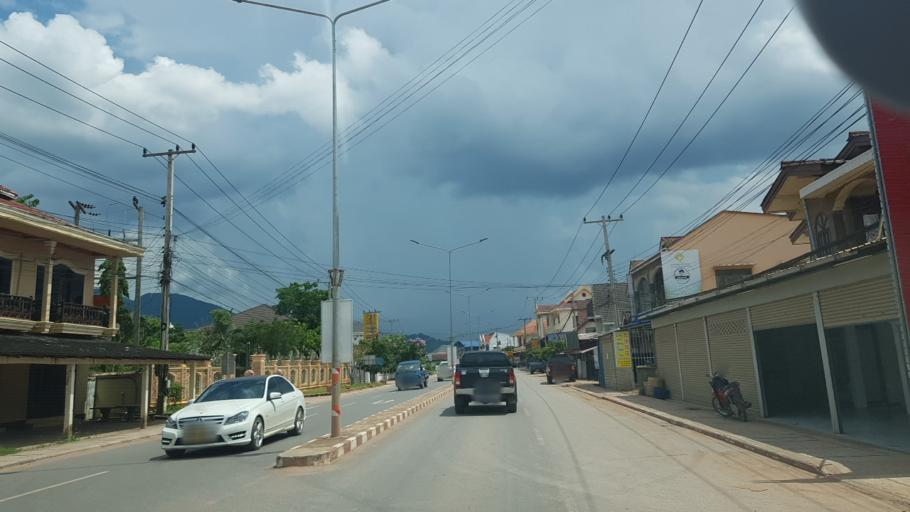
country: LA
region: Oudomxai
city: Muang Xay
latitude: 20.6822
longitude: 101.9866
